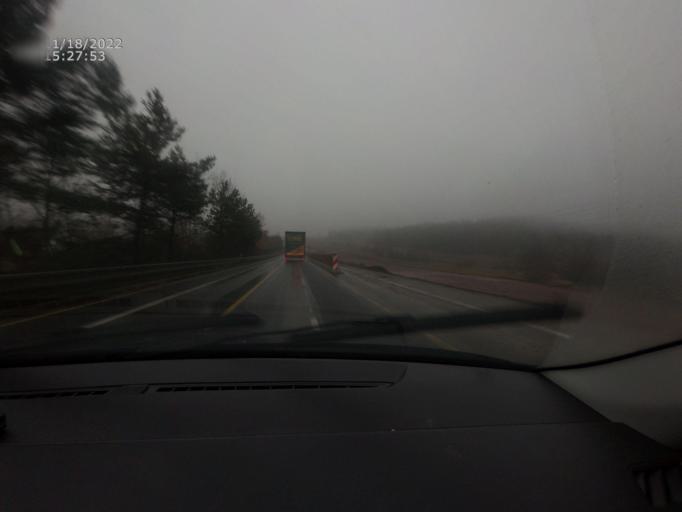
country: CZ
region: Central Bohemia
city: Milin
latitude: 49.6301
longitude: 14.0515
